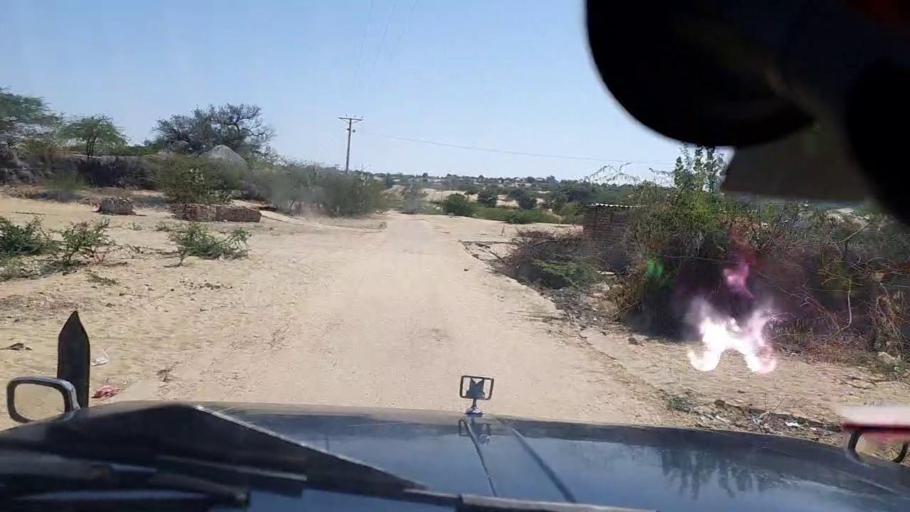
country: PK
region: Sindh
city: Diplo
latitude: 24.5670
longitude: 69.6827
